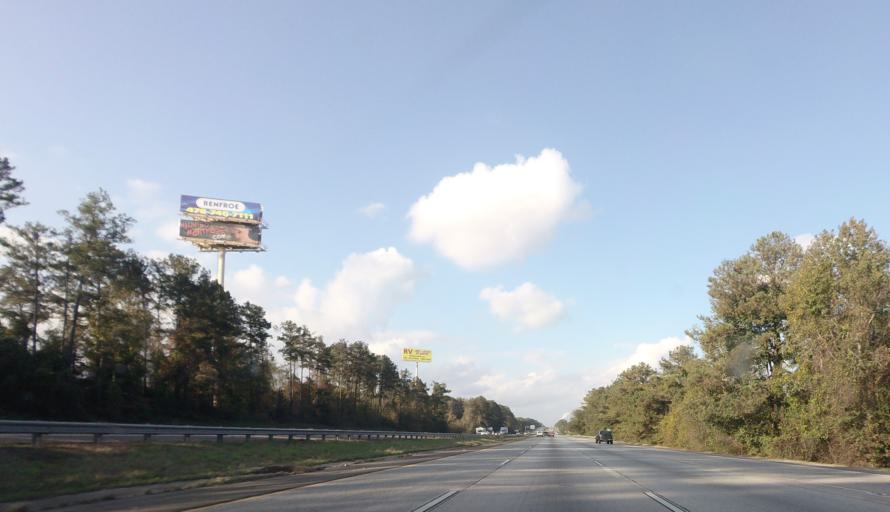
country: US
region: Georgia
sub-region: Peach County
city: Byron
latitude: 32.6165
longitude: -83.7428
